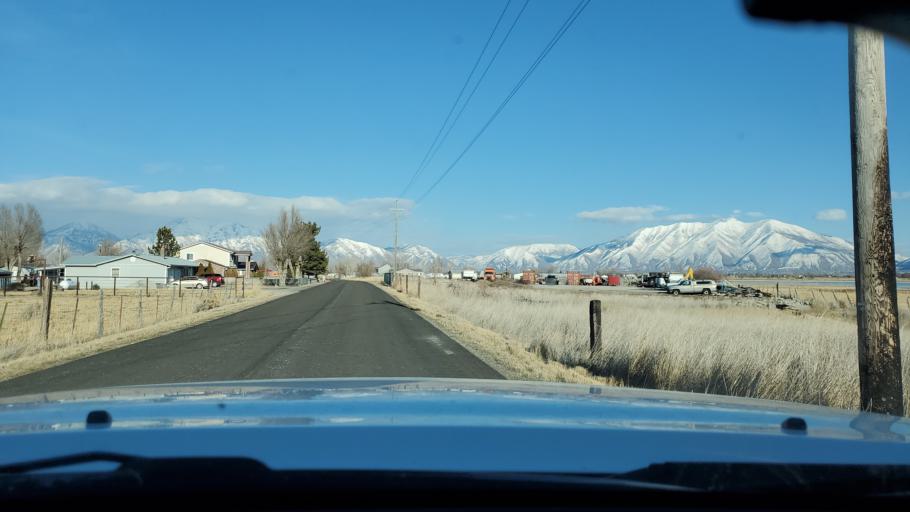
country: US
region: Utah
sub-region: Utah County
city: Benjamin
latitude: 40.1149
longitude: -111.7804
